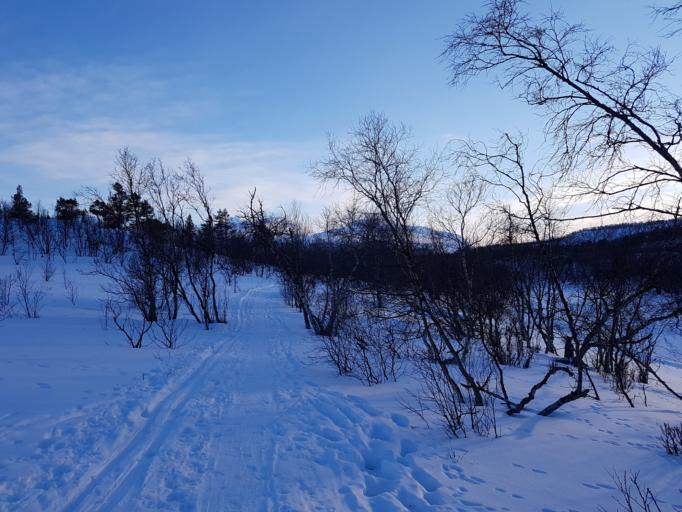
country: NO
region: Troms
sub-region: Bardu
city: Setermoen
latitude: 68.3476
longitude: 18.7672
